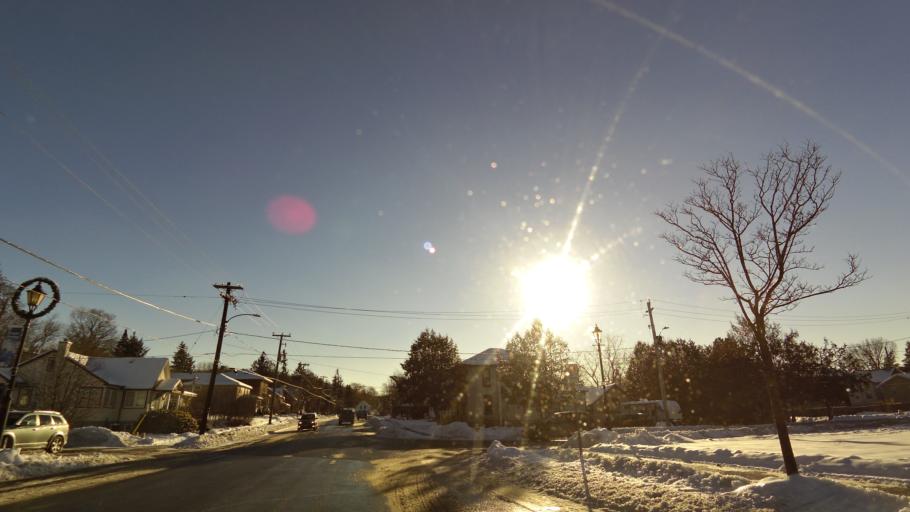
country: CA
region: Ontario
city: Quinte West
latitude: 44.3068
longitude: -77.7967
